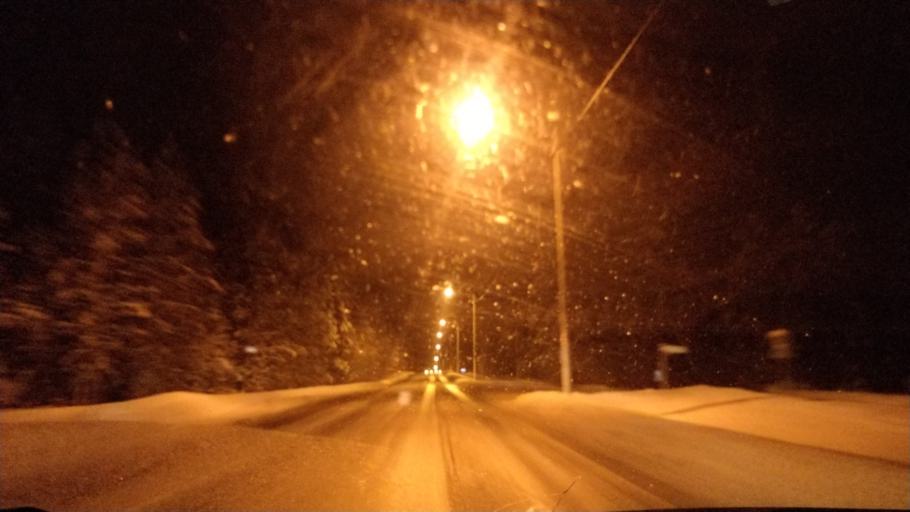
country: FI
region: Lapland
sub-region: Rovaniemi
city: Rovaniemi
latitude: 66.3218
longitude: 25.3576
